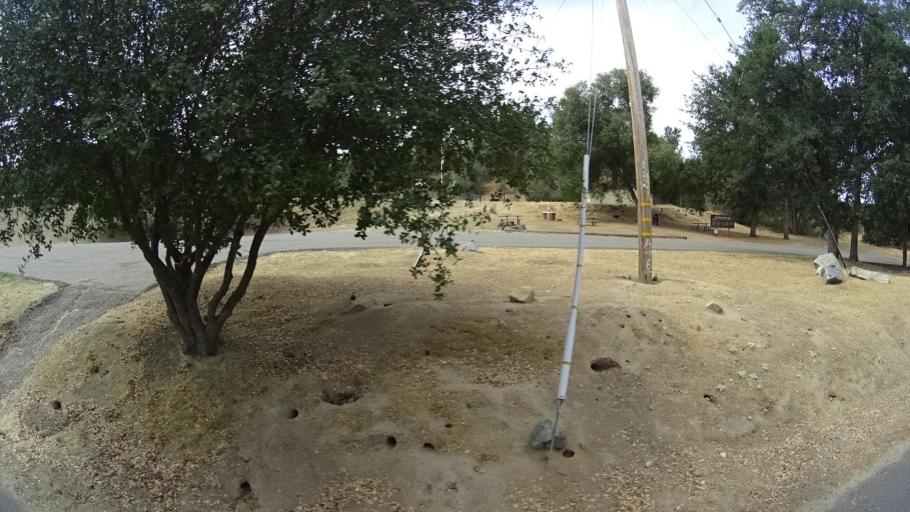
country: US
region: California
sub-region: Mariposa County
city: Midpines
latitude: 37.4499
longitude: -119.8498
